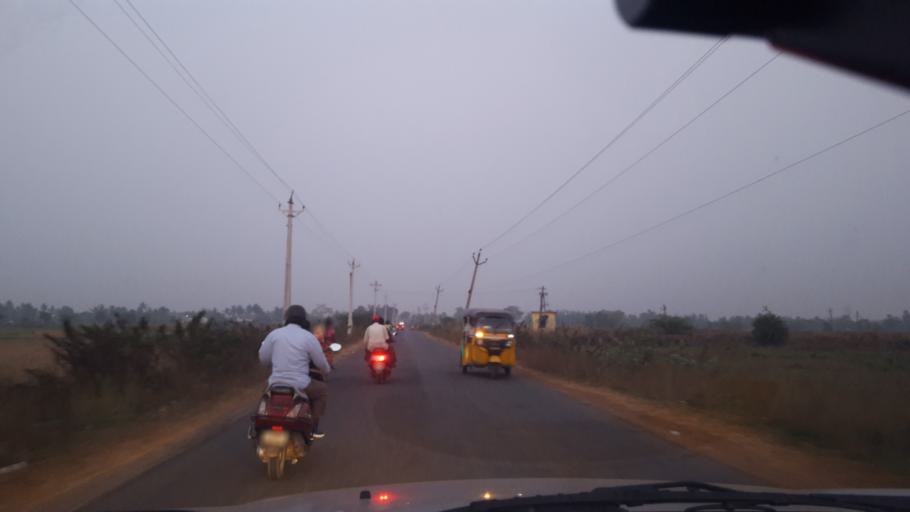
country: IN
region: Andhra Pradesh
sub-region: Srikakulam
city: Palasa
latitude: 18.7304
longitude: 84.3950
